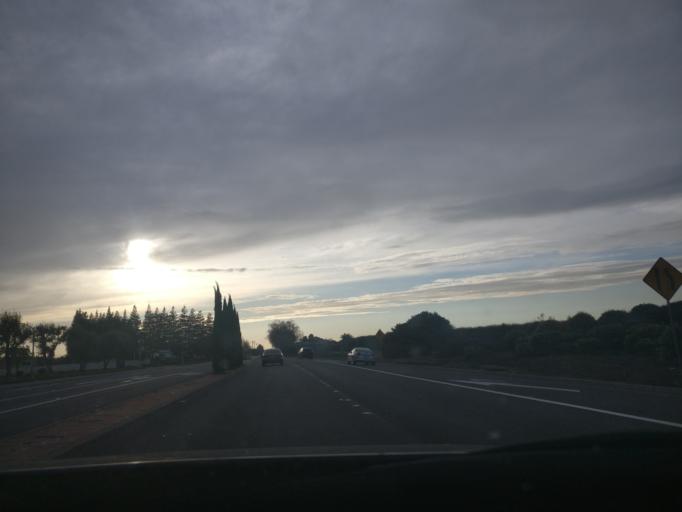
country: US
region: California
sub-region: Alameda County
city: Cherryland
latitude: 37.6533
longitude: -122.1105
